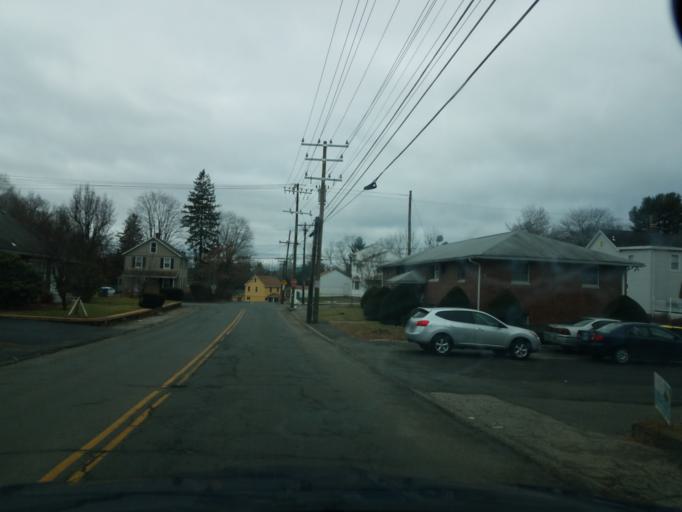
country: US
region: Connecticut
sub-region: New Haven County
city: Waterbury
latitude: 41.5361
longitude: -73.0233
